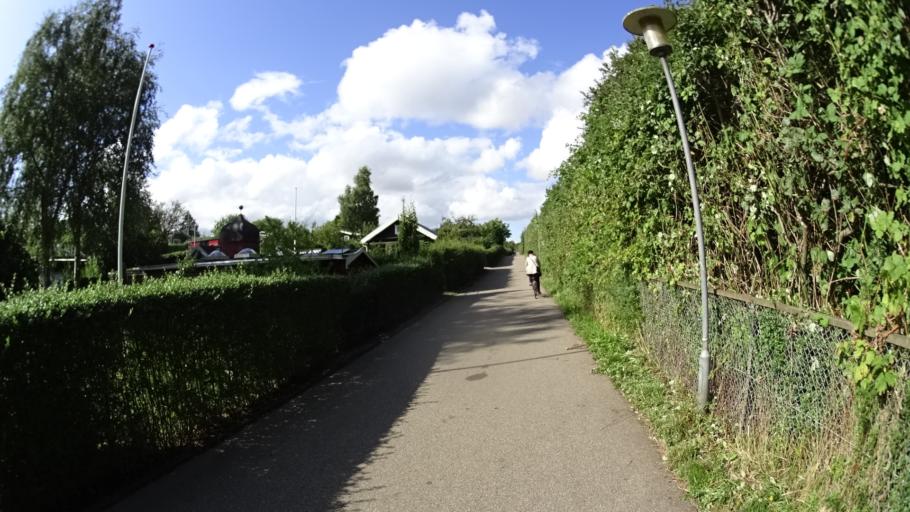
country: DK
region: Central Jutland
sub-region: Arhus Kommune
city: Arhus
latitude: 56.1592
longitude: 10.1777
